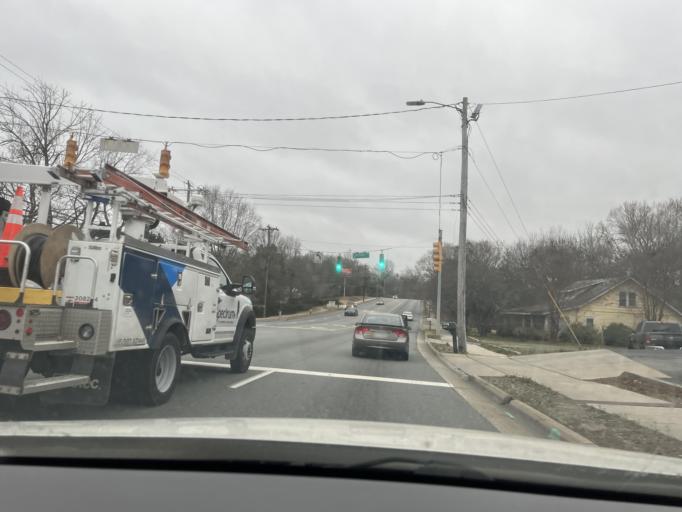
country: US
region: North Carolina
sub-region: Guilford County
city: Greensboro
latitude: 36.0243
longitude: -79.8024
